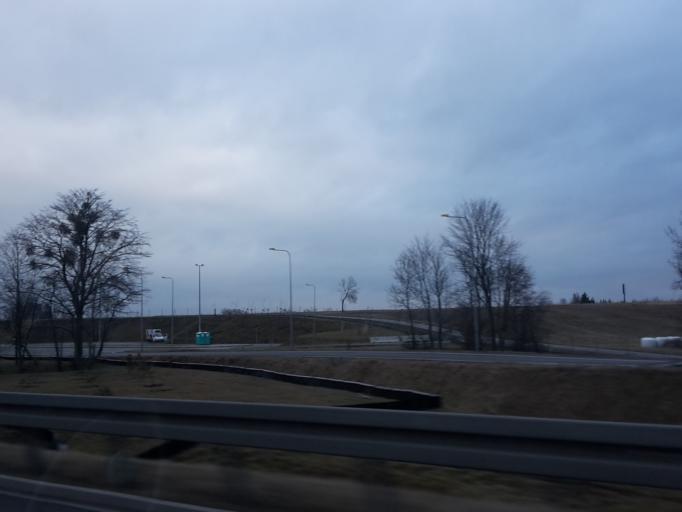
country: PL
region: Warmian-Masurian Voivodeship
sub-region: Powiat ostrodzki
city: Milomlyn
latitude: 53.8048
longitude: 19.7892
